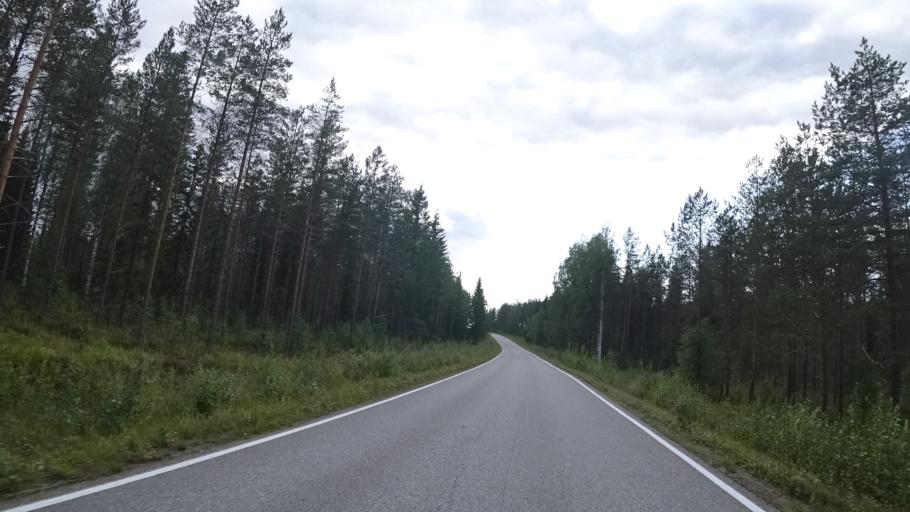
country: FI
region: North Karelia
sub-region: Joensuu
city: Ilomantsi
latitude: 62.4349
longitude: 31.0589
